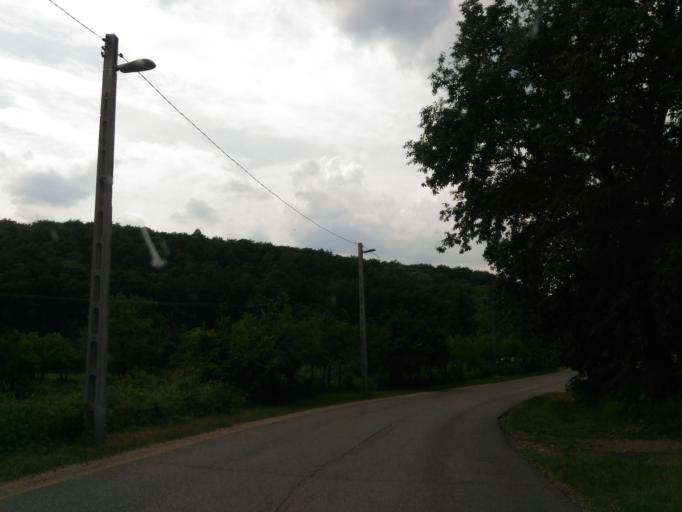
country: HU
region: Baranya
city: Komlo
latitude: 46.1855
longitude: 18.2527
